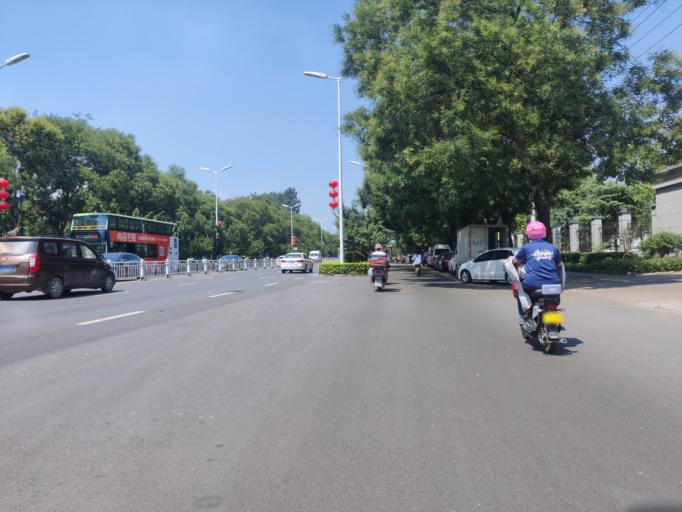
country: CN
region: Henan Sheng
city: Puyang
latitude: 35.7730
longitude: 115.0134
